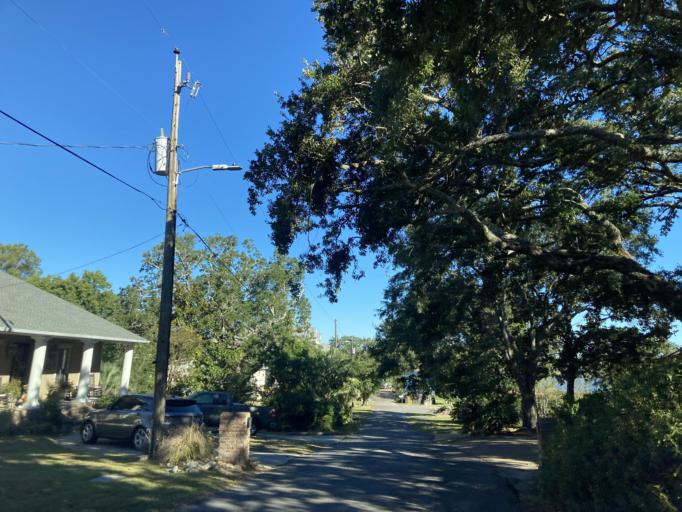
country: US
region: Mississippi
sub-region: Jackson County
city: Ocean Springs
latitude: 30.4177
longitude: -88.8369
